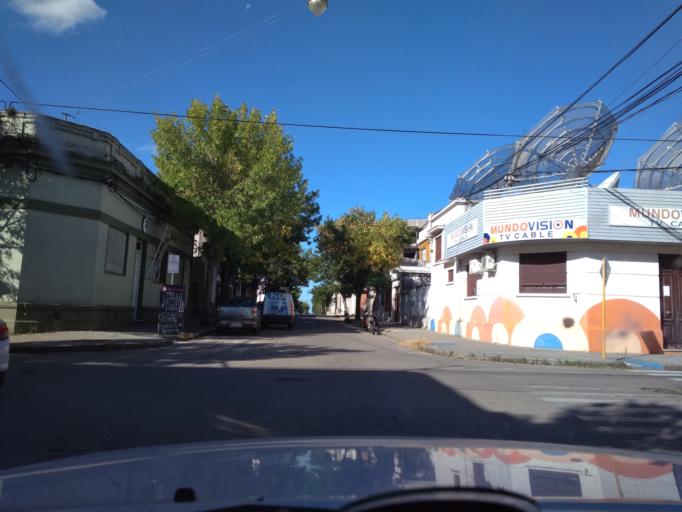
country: UY
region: Florida
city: Florida
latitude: -34.0965
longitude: -56.2164
